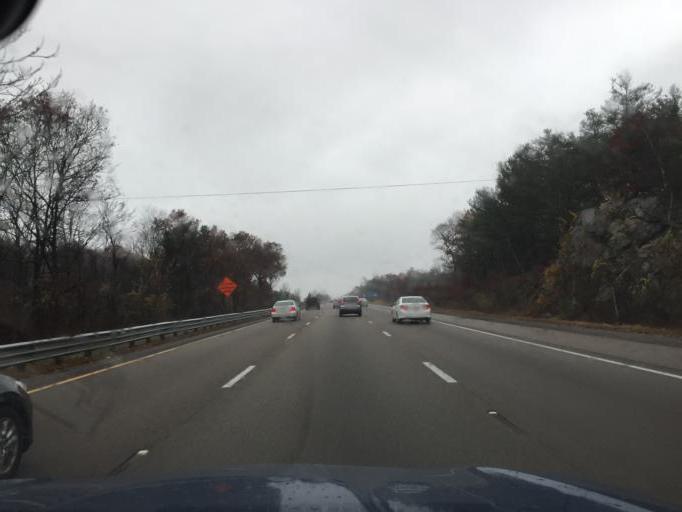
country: US
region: Massachusetts
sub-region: Norfolk County
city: Foxborough
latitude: 42.0589
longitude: -71.2331
